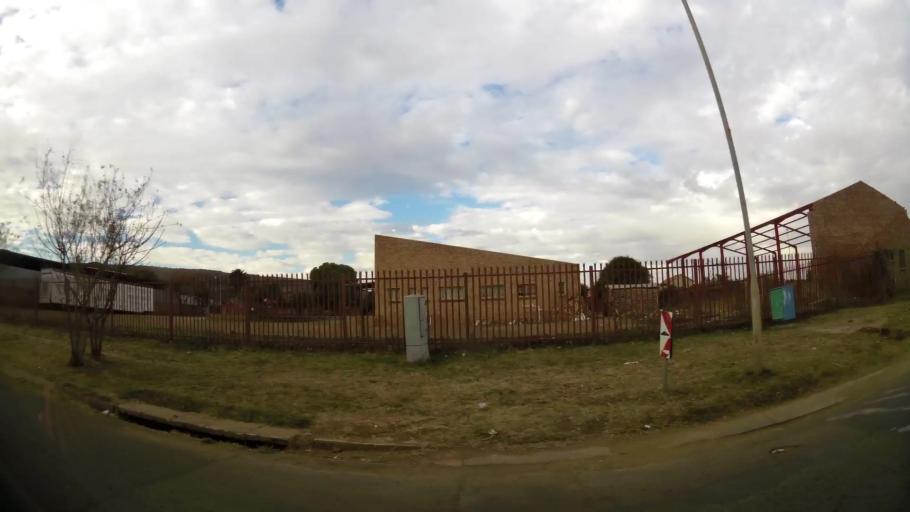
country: ZA
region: Gauteng
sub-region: City of Tshwane Metropolitan Municipality
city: Pretoria
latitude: -25.7049
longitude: 28.3055
